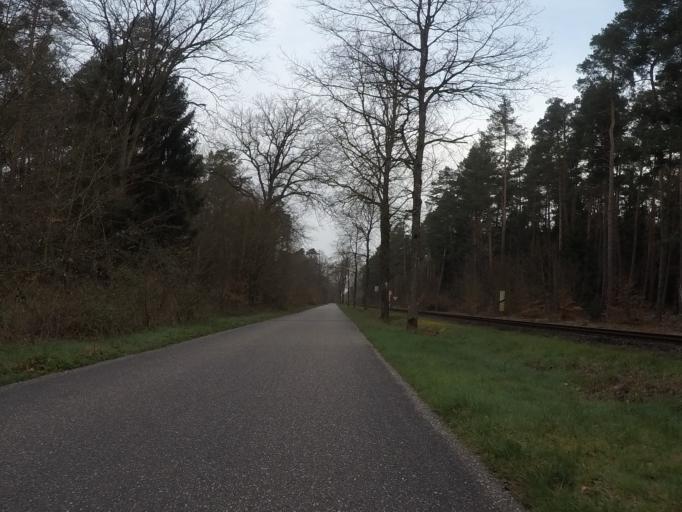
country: DE
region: Rheinland-Pfalz
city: Kandel
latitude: 49.0702
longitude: 8.2213
